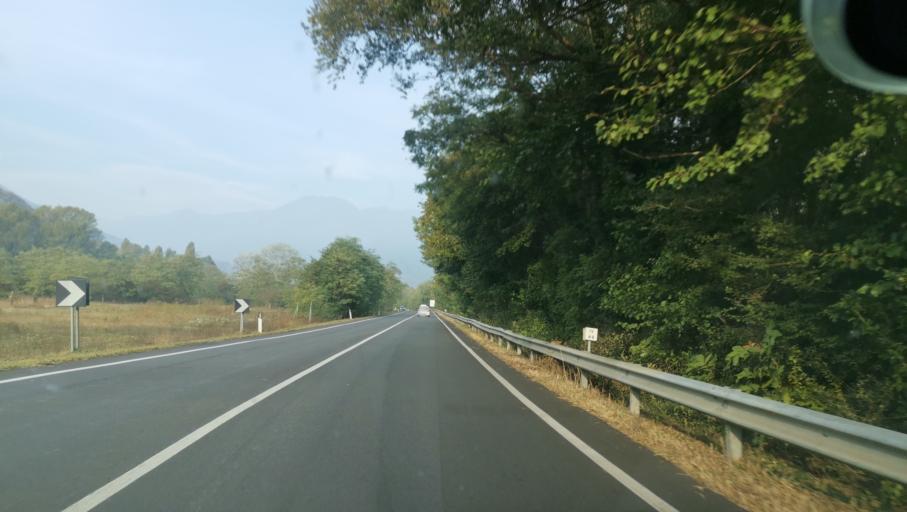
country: IT
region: Piedmont
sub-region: Provincia di Torino
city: Mattie
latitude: 45.1315
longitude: 7.1235
